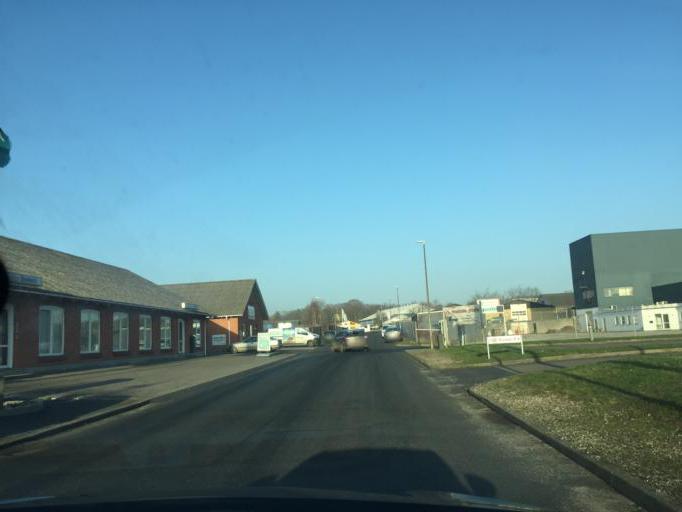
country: DK
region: South Denmark
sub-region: Faaborg-Midtfyn Kommune
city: Faaborg
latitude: 55.1085
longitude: 10.2356
